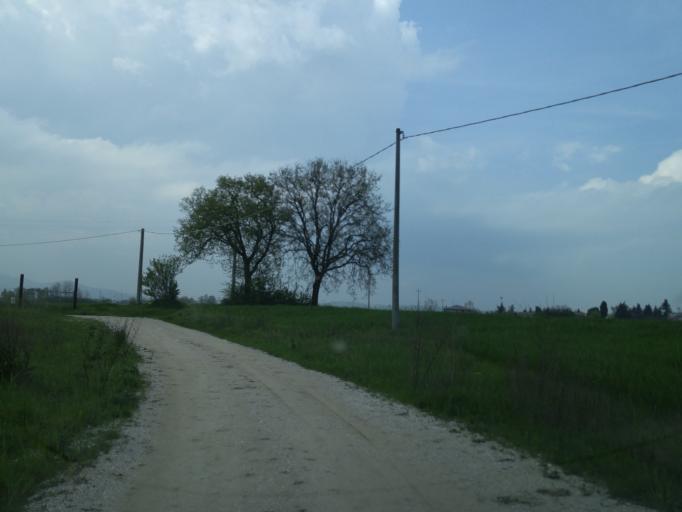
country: IT
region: The Marches
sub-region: Provincia di Pesaro e Urbino
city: Cuccurano
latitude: 43.7692
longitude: 12.9706
